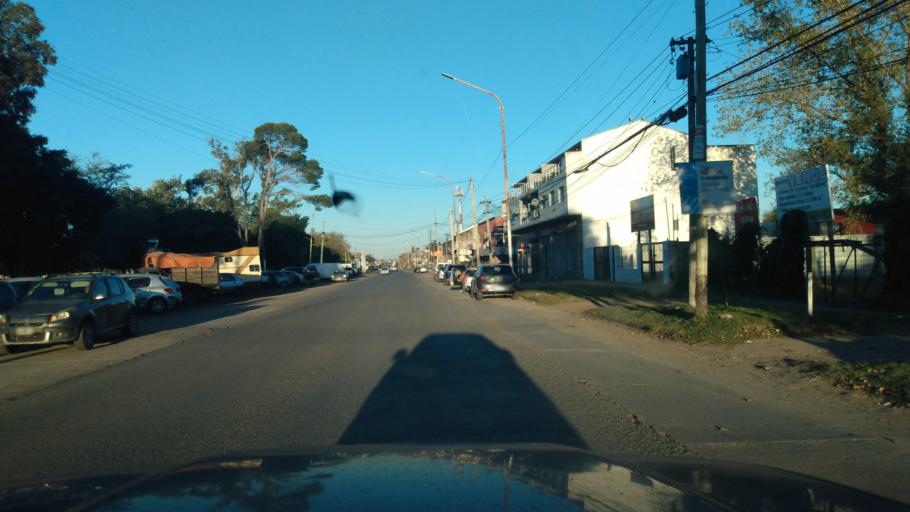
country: AR
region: Buenos Aires
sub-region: Partido de Merlo
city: Merlo
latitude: -34.6538
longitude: -58.7731
